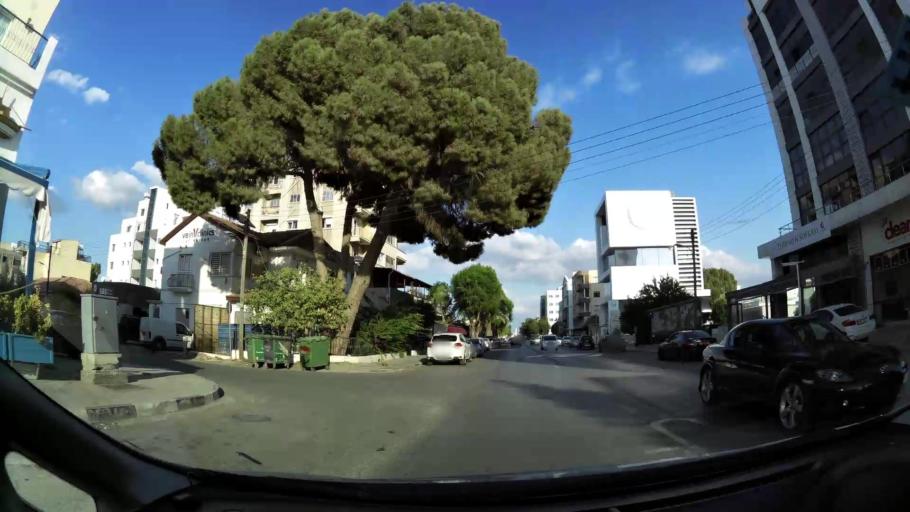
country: CY
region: Lefkosia
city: Nicosia
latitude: 35.1902
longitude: 33.3608
